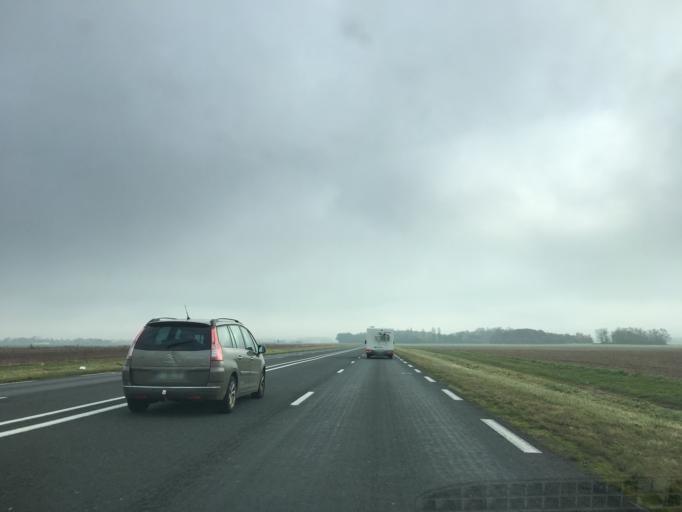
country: FR
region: Ile-de-France
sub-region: Departement de Seine-et-Marne
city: Perthes
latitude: 48.4608
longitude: 2.5693
